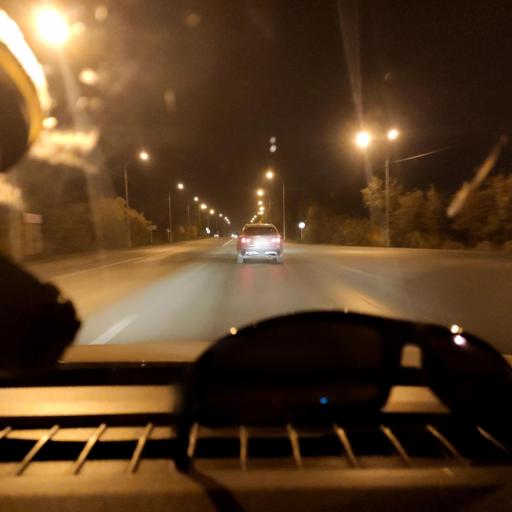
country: RU
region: Samara
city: Samara
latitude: 53.0808
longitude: 50.0927
